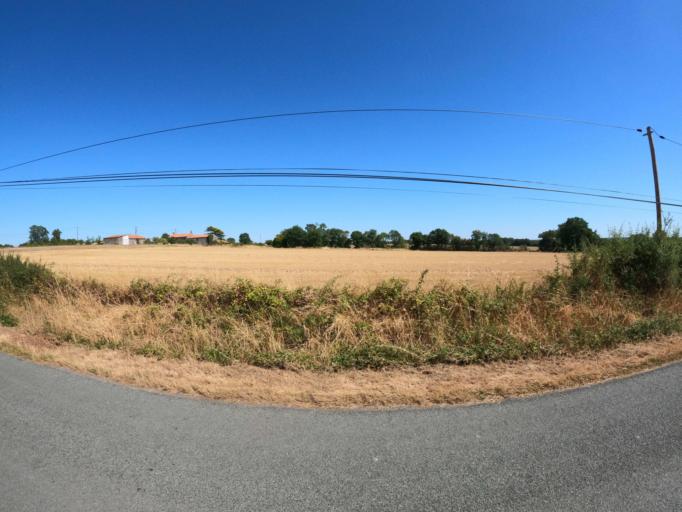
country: FR
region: Pays de la Loire
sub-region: Departement de la Vendee
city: Saint-Aubin-des-Ormeaux
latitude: 47.0139
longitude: -0.9974
